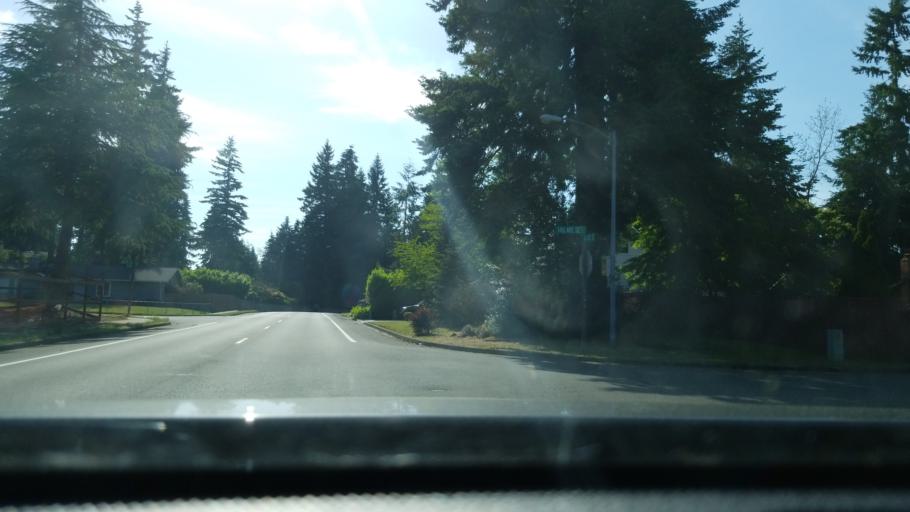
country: US
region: Washington
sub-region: King County
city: Fairwood
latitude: 47.4757
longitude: -122.1455
